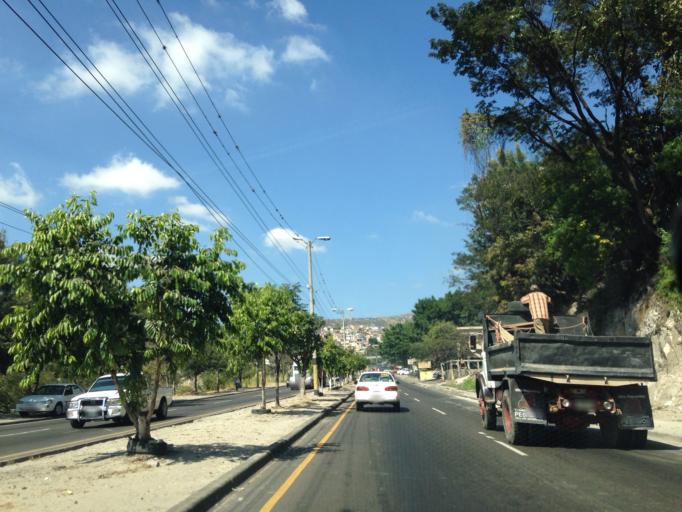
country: HN
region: Francisco Morazan
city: Tegucigalpa
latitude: 14.0877
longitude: -87.2348
